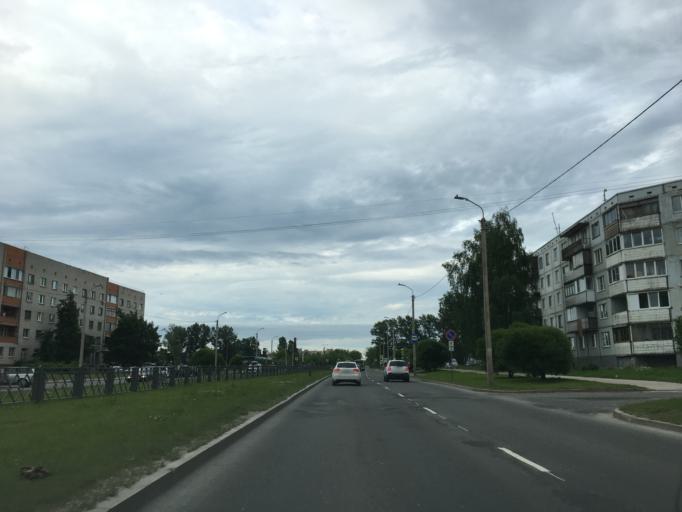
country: RU
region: Pskov
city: Pskov
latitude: 57.8375
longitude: 28.3032
